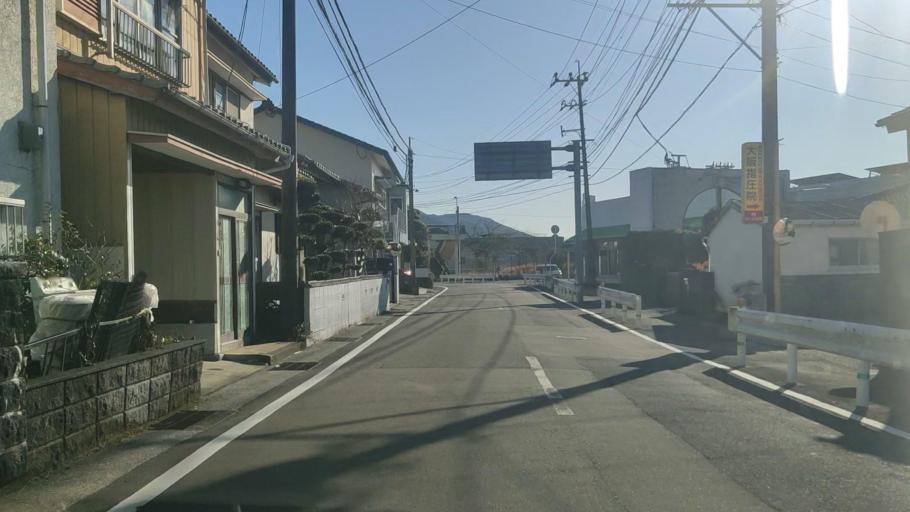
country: JP
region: Miyazaki
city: Nobeoka
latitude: 32.6099
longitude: 131.6840
